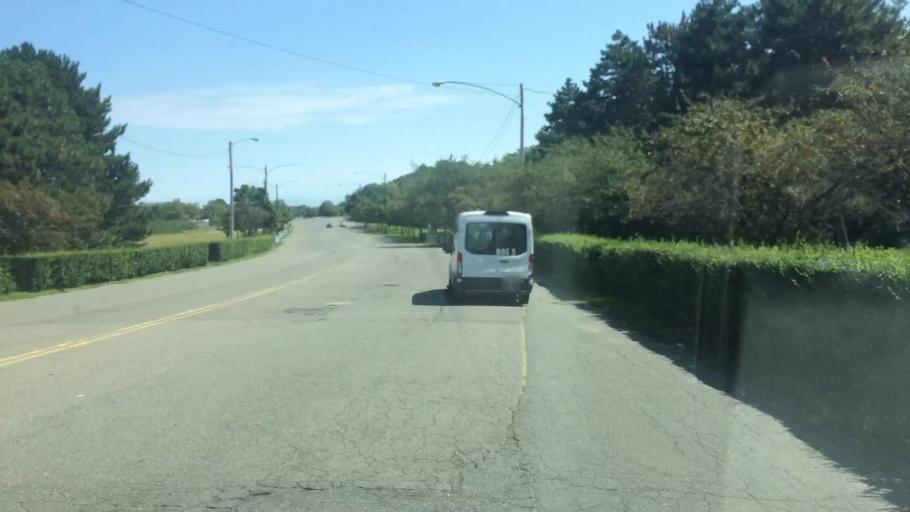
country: US
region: Massachusetts
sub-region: Suffolk County
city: Revere
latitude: 42.3942
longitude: -71.0098
